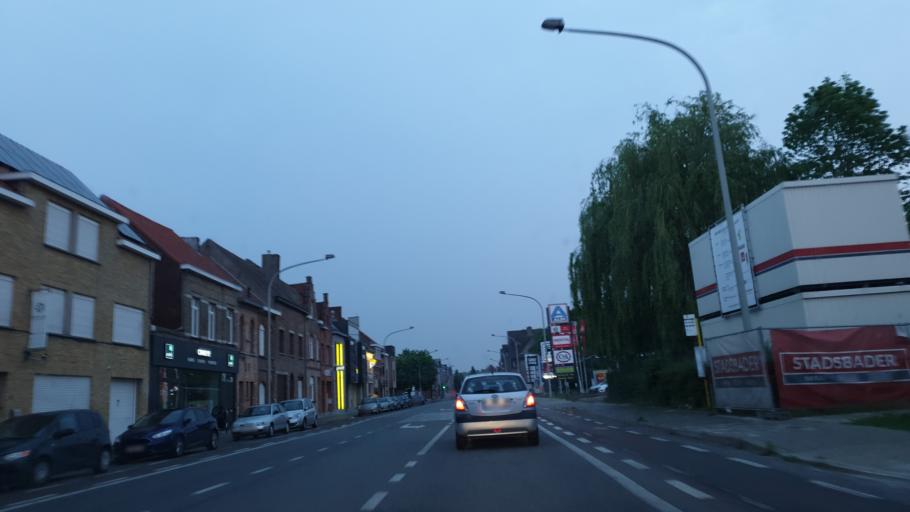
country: BE
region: Flanders
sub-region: Provincie West-Vlaanderen
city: Ieper
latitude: 50.8540
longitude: 2.8743
